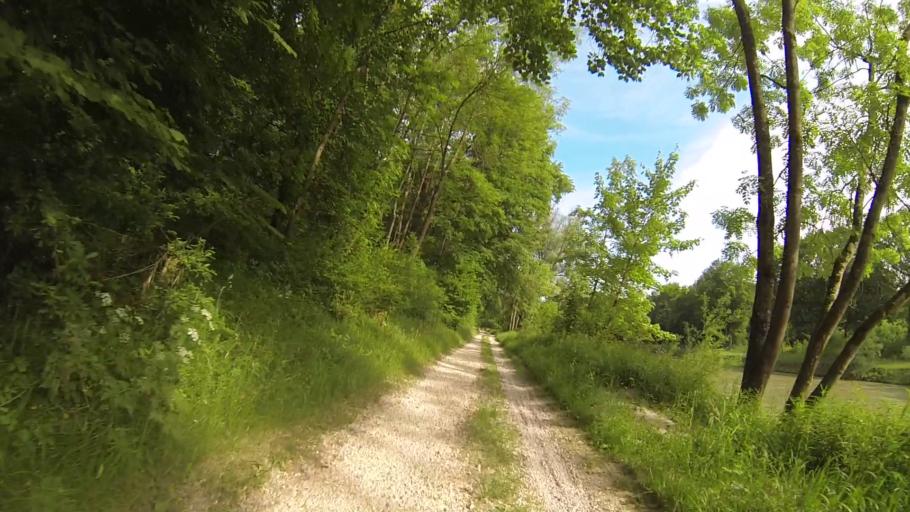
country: DE
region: Bavaria
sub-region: Swabia
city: Neu-Ulm
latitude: 48.3497
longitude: 10.0003
